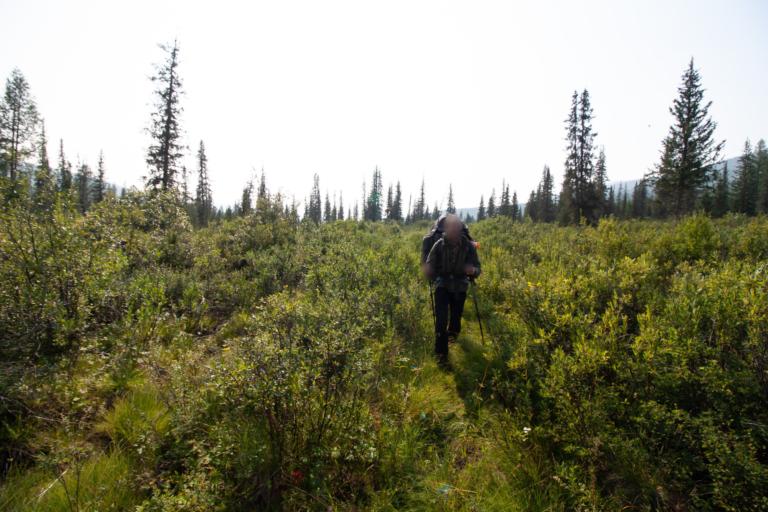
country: RU
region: Respublika Buryatiya
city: Nizhneangarsk
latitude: 56.2135
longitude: 109.7075
